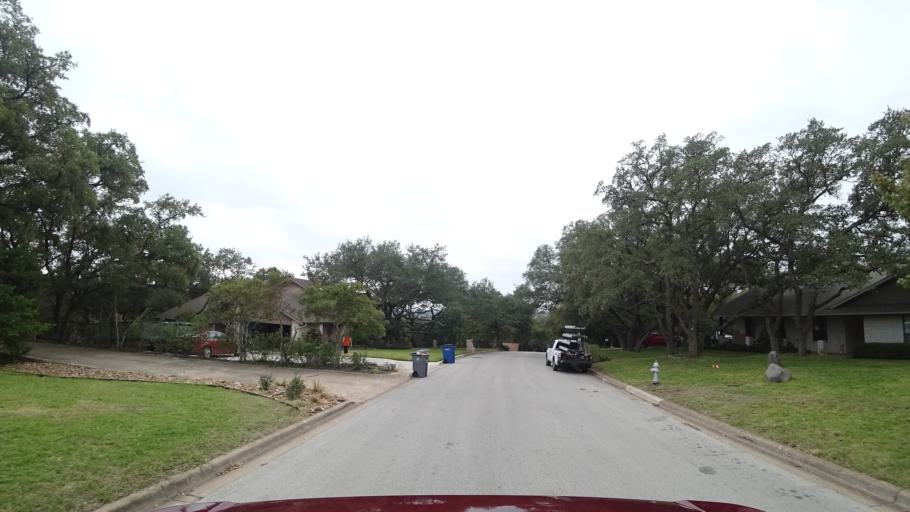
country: US
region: Texas
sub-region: Williamson County
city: Anderson Mill
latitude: 30.4419
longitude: -97.8132
